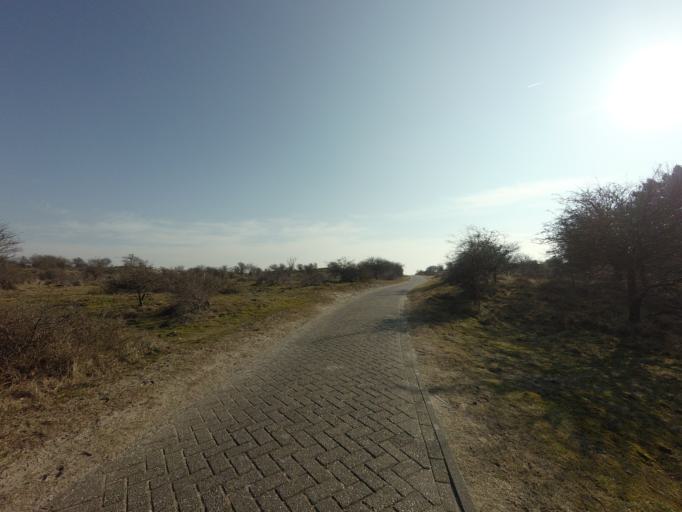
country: NL
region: North Holland
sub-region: Gemeente Bloemendaal
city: Bloemendaal
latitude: 52.4264
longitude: 4.5848
